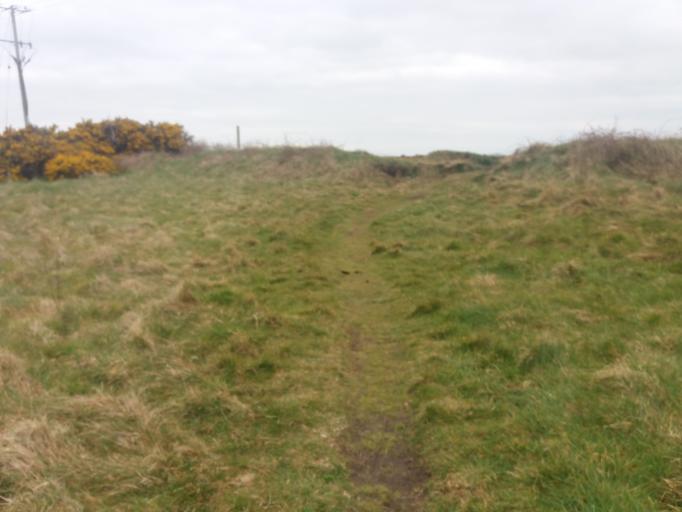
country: IE
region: Leinster
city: Portmarnock
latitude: 53.4214
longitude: -6.1312
